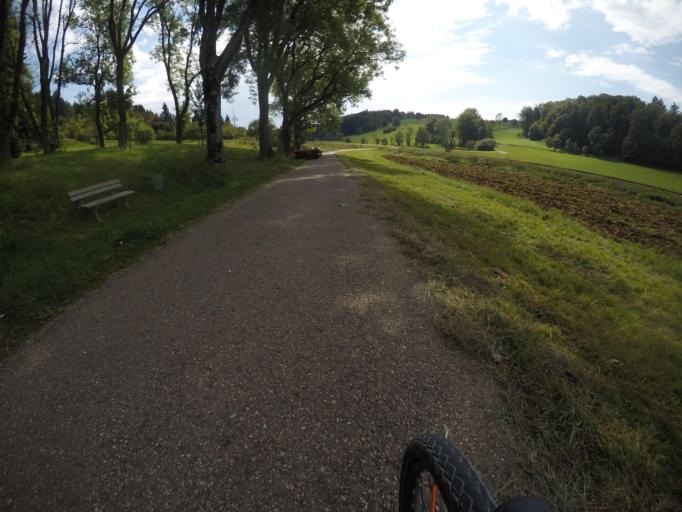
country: DE
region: Baden-Wuerttemberg
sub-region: Tuebingen Region
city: Munsingen
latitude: 48.4012
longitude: 9.4951
